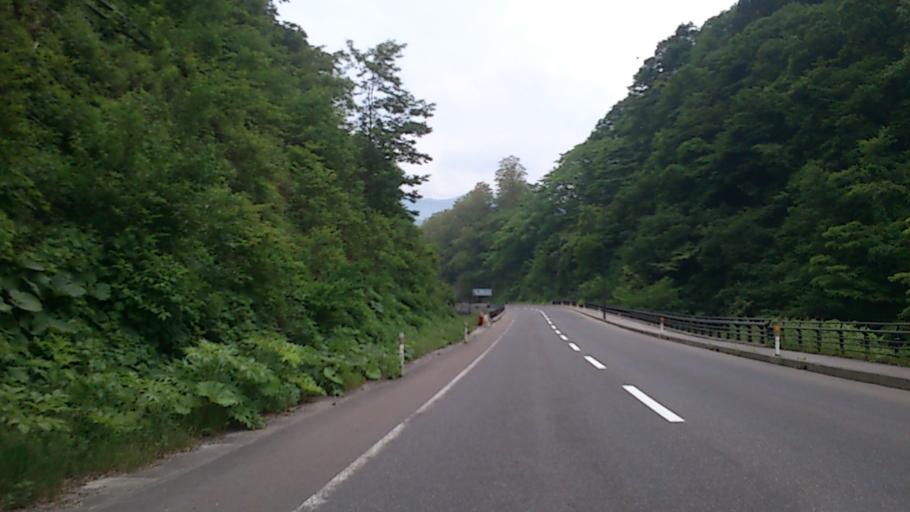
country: JP
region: Aomori
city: Hirosaki
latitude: 40.5626
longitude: 140.2841
